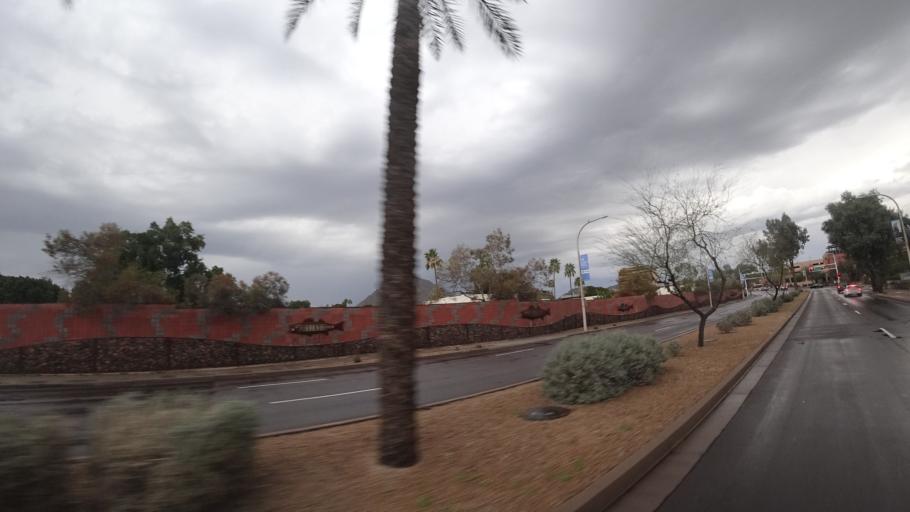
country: US
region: Arizona
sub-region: Maricopa County
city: Scottsdale
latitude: 33.4987
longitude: -111.9302
